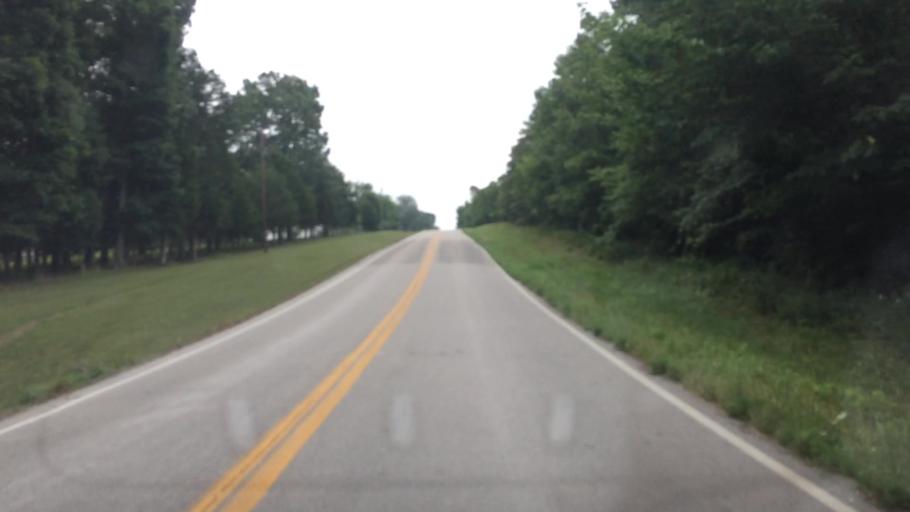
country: US
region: Missouri
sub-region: Webster County
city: Marshfield
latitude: 37.3414
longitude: -93.0087
